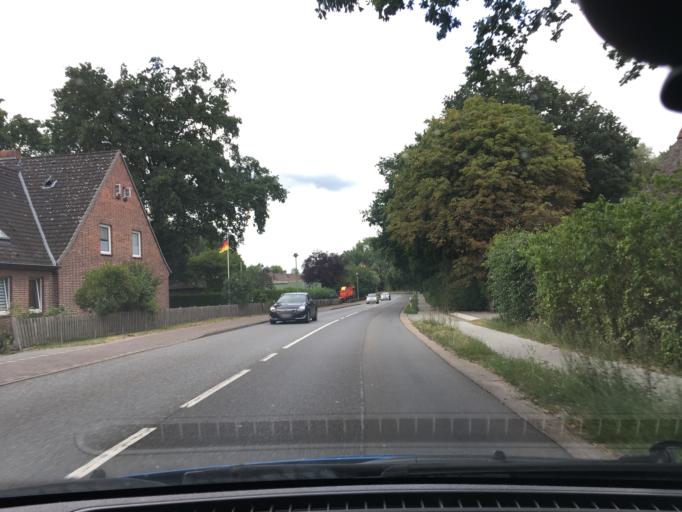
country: DE
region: Lower Saxony
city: Neu Wulmstorf
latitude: 53.4464
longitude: 9.7572
